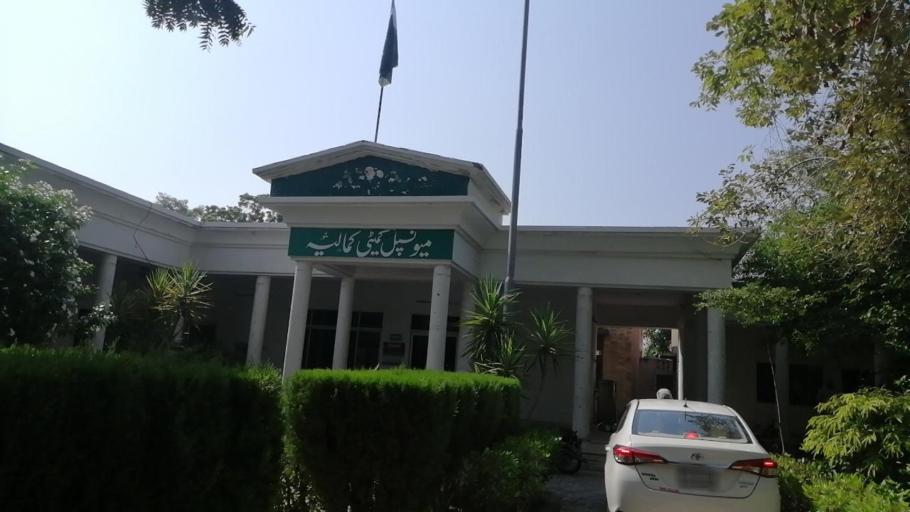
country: PK
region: Punjab
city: Kamalia
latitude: 30.7252
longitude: 72.6486
